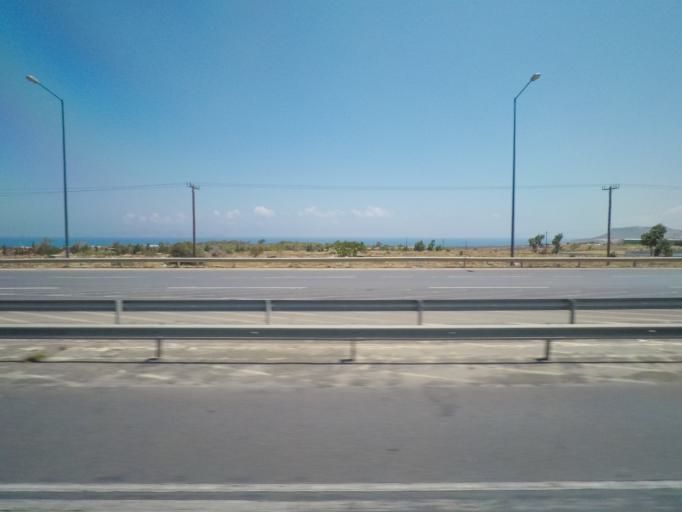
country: GR
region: Crete
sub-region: Nomos Irakleiou
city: Nea Alikarnassos
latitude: 35.3277
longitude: 25.1772
